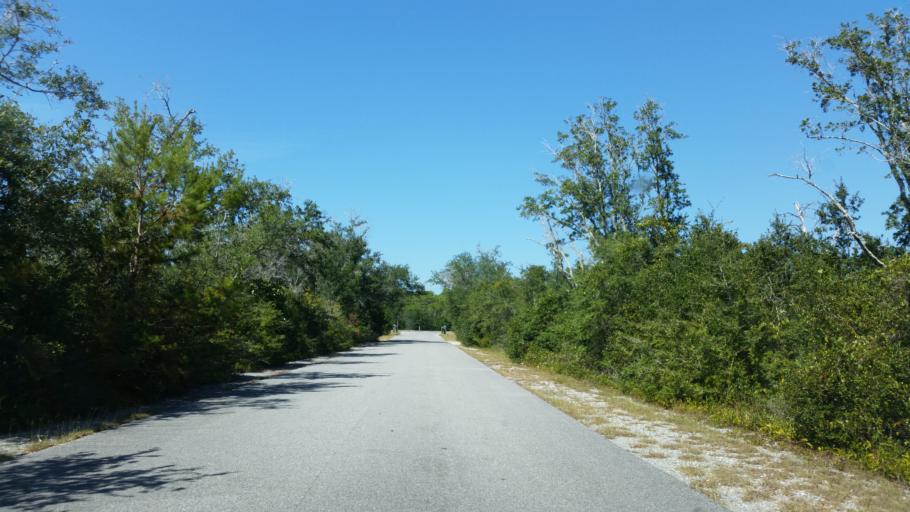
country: US
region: Florida
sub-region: Santa Rosa County
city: Oriole Beach
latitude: 30.3655
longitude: -87.1267
